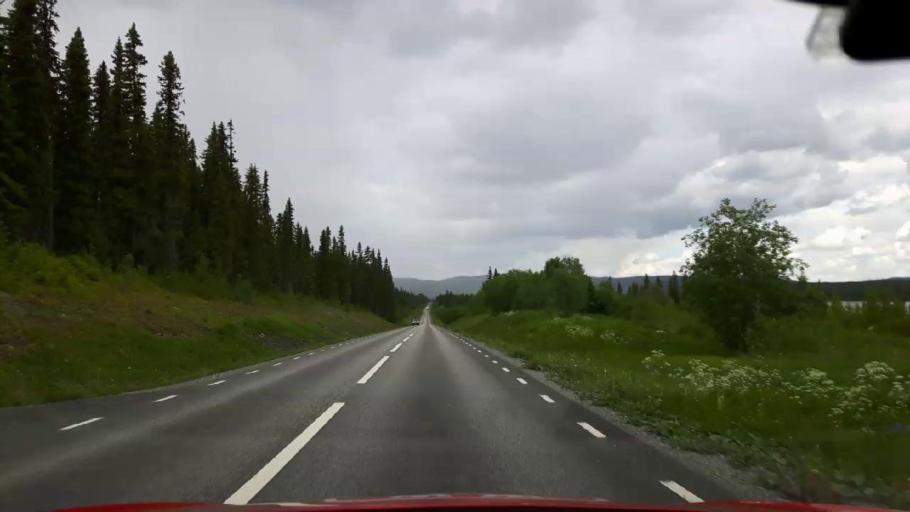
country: SE
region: Jaemtland
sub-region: Krokoms Kommun
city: Krokom
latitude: 63.7056
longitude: 14.3127
